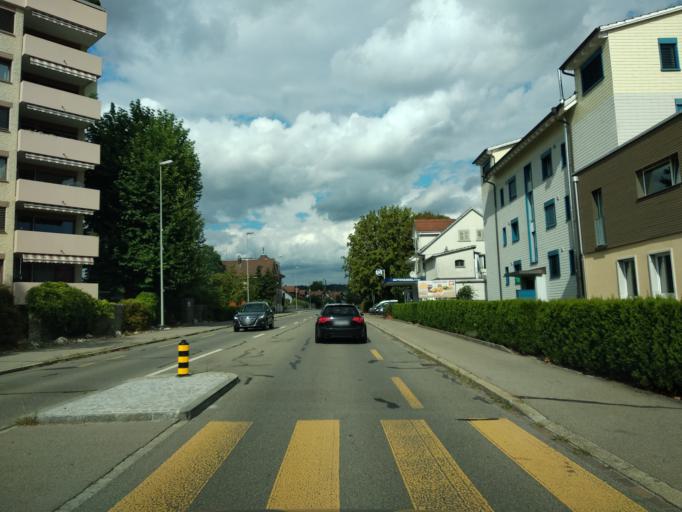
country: CH
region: Zurich
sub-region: Bezirk Uster
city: Bruttisellen
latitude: 47.4246
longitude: 8.6323
